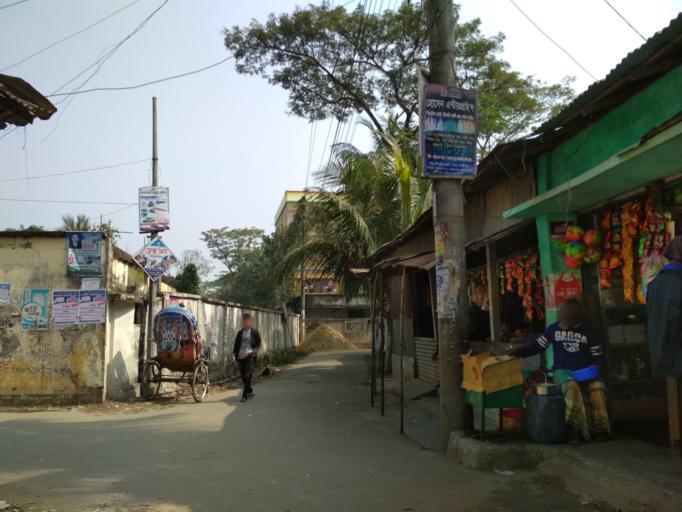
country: BD
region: Chittagong
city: Lakshmipur
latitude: 22.9310
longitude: 90.8259
